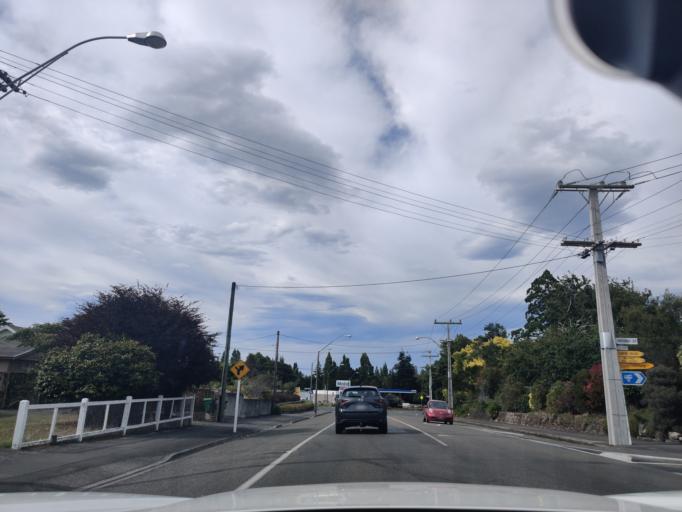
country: NZ
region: Wellington
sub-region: Masterton District
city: Masterton
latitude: -40.9439
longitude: 175.6695
